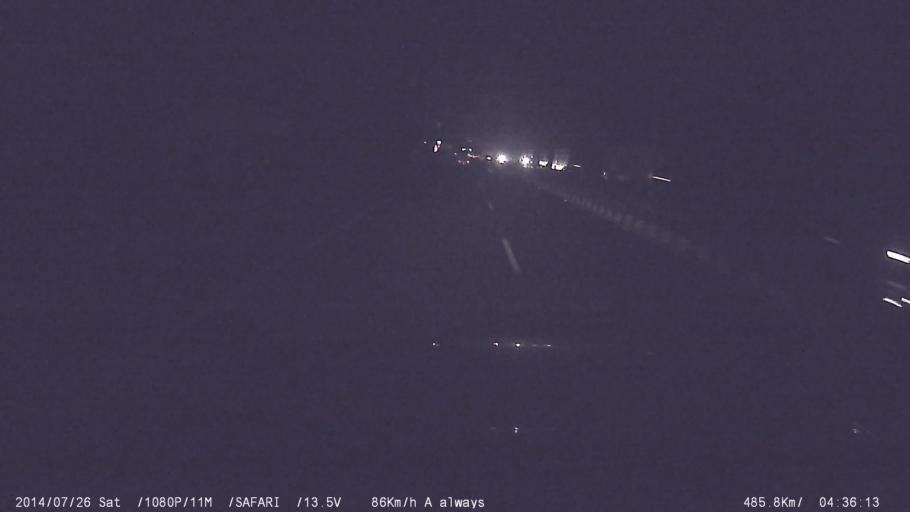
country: IN
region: Kerala
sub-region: Thrissur District
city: Kizhake Chalakudi
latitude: 10.2619
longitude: 76.3570
